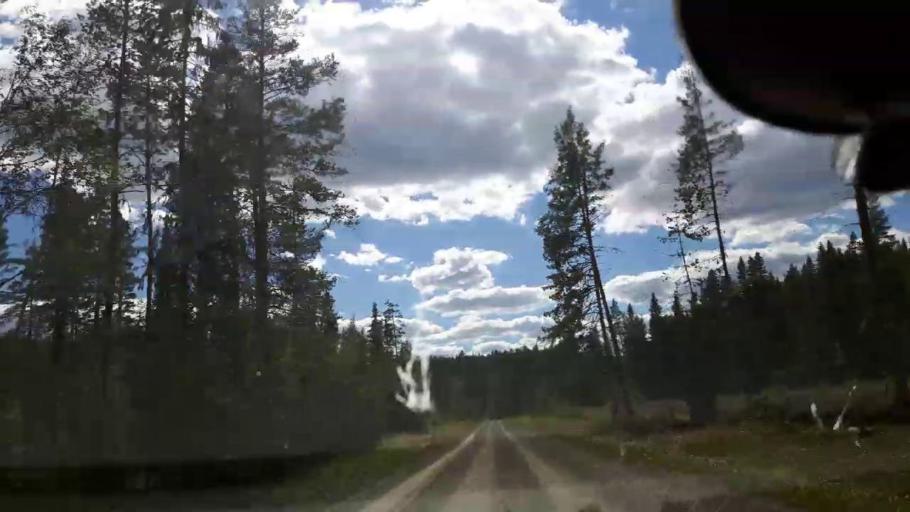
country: SE
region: Vaesternorrland
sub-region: Ange Kommun
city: Fransta
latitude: 62.7743
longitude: 15.9358
